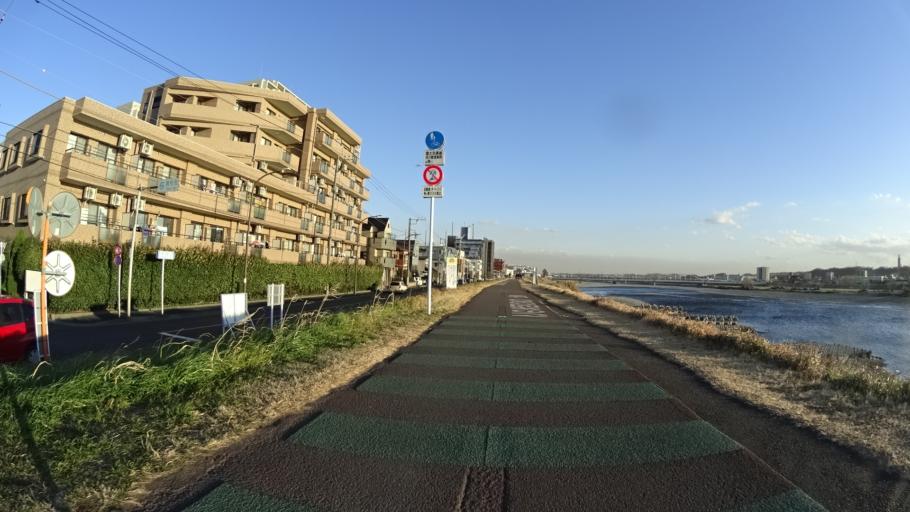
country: JP
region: Tokyo
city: Chofugaoka
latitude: 35.6500
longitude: 139.5207
